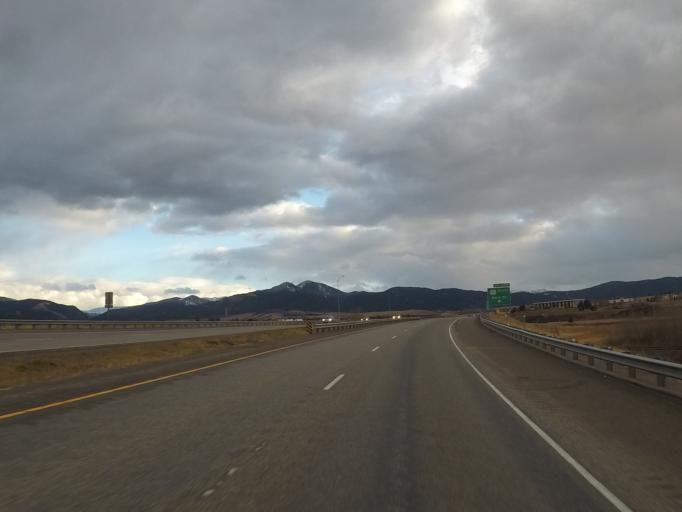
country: US
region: Montana
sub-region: Gallatin County
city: Bozeman
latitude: 45.6814
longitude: -111.0124
